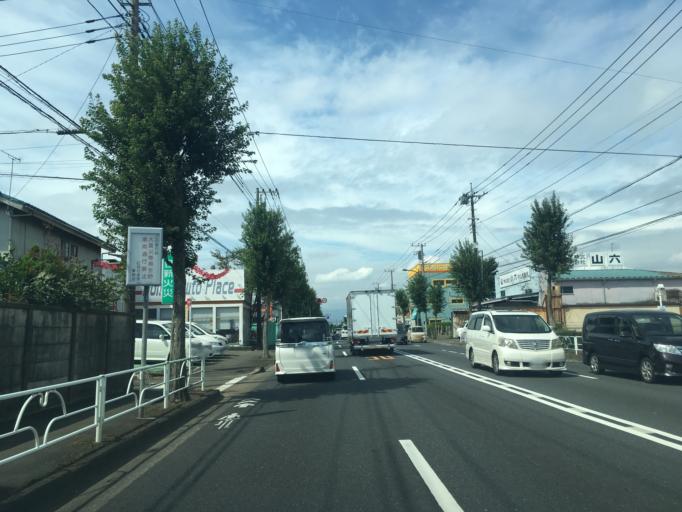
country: JP
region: Tokyo
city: Higashimurayama-shi
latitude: 35.7489
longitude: 139.4012
